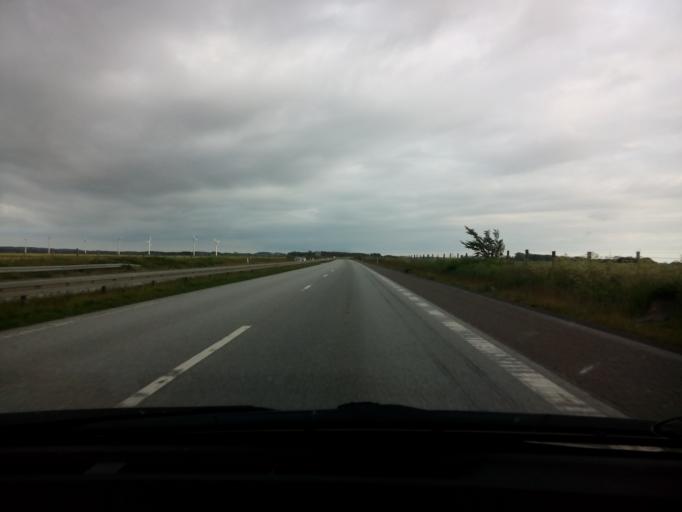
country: DK
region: North Denmark
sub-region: Hjorring Kommune
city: Hjorring
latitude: 57.4140
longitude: 10.0289
